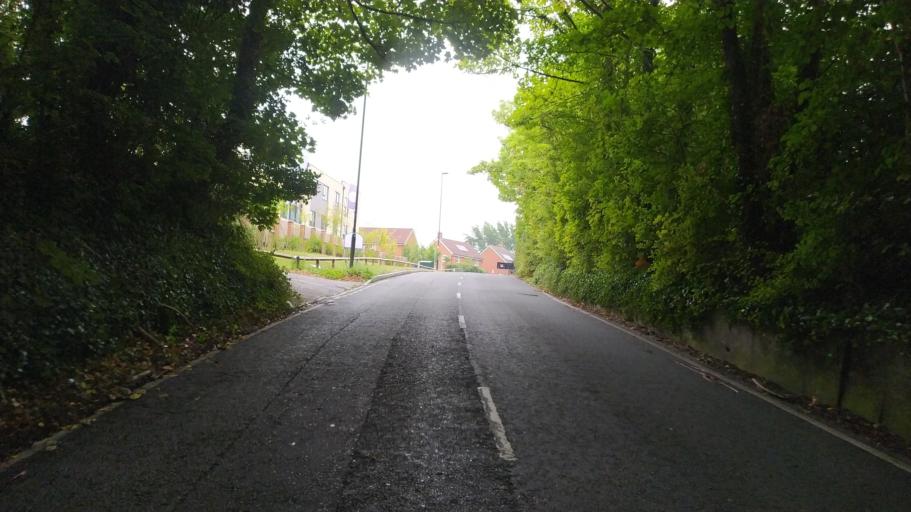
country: GB
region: England
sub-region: Hampshire
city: West End
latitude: 50.9372
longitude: -1.3556
